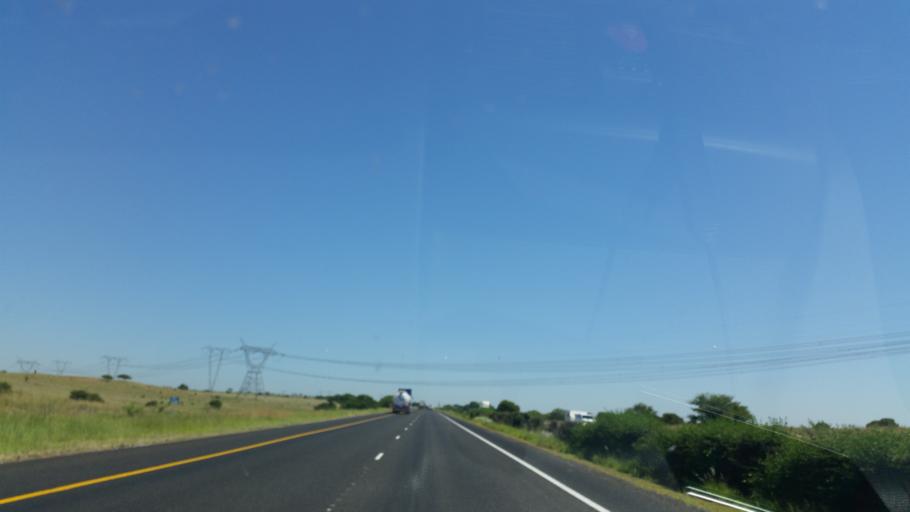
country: ZA
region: KwaZulu-Natal
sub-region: uThukela District Municipality
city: Ladysmith
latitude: -28.6626
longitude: 29.6315
